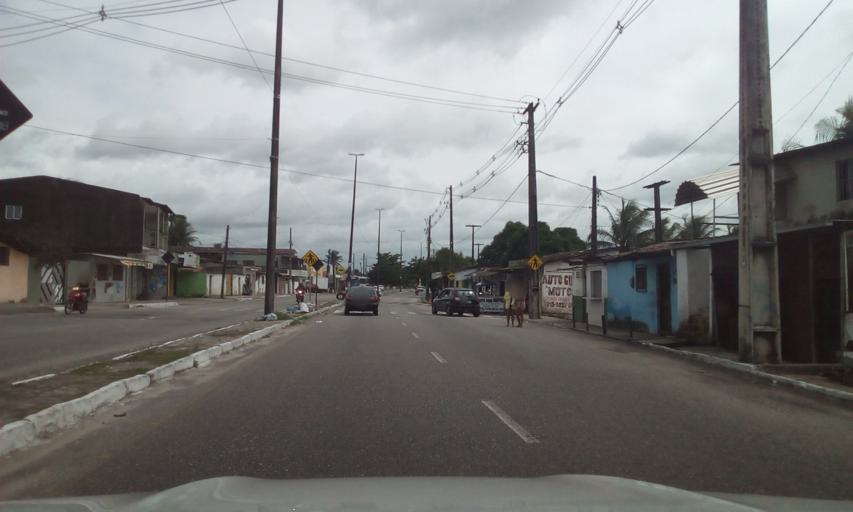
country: BR
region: Paraiba
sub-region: Bayeux
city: Bayeux
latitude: -7.1235
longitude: -34.8975
